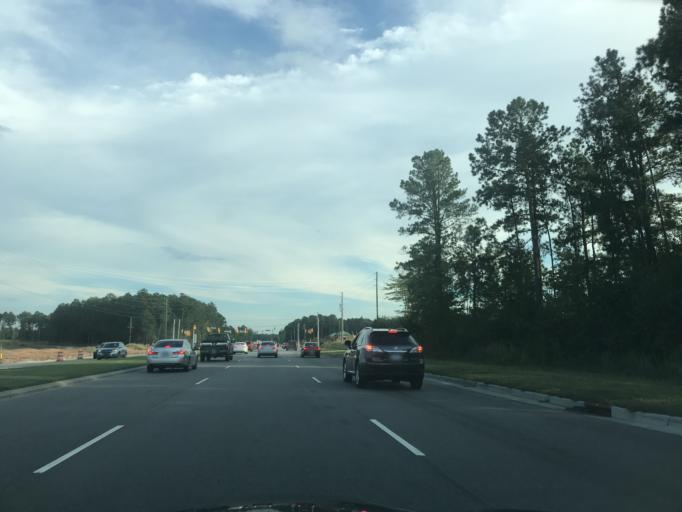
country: US
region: North Carolina
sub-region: Wake County
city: Green Level
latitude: 35.8371
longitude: -78.8836
